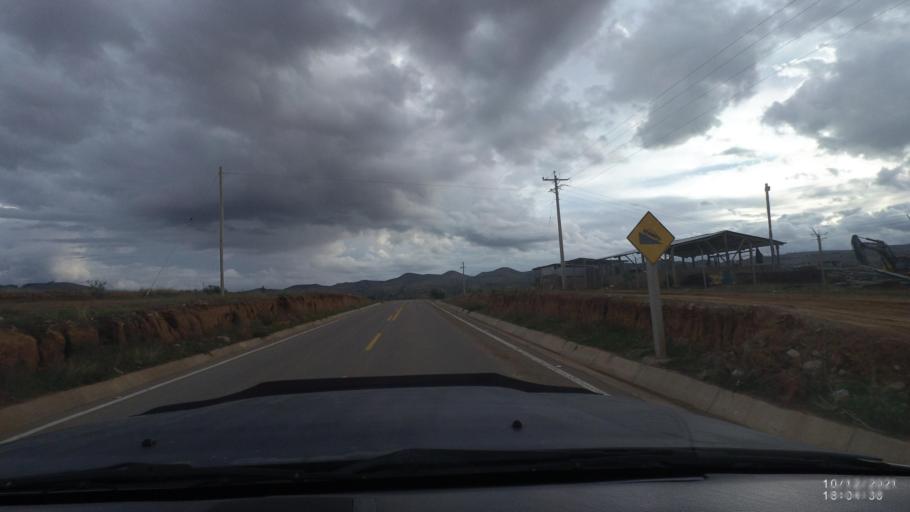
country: BO
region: Cochabamba
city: Cliza
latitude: -17.7697
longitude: -65.9267
